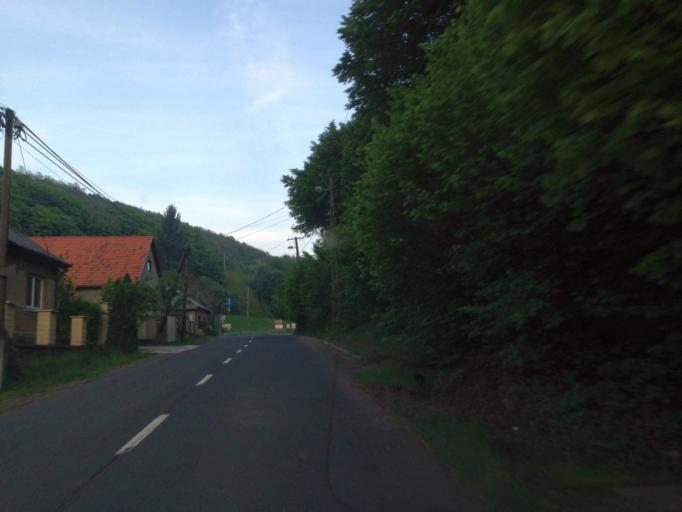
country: HU
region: Nograd
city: Batonyterenye
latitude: 47.9007
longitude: 19.8149
